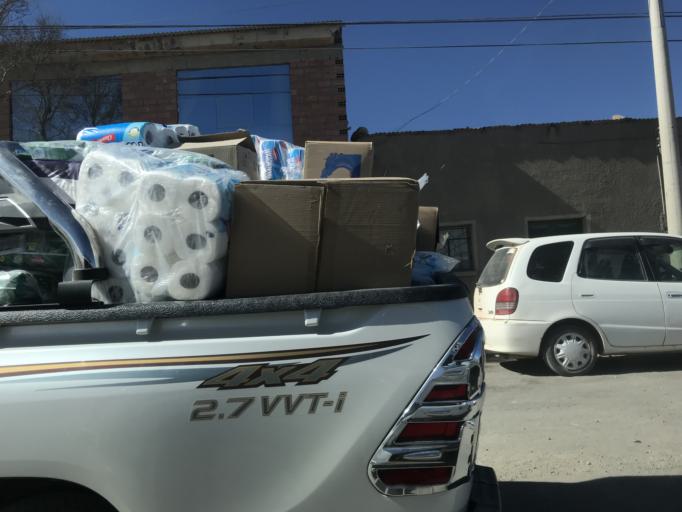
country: BO
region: Potosi
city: Uyuni
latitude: -20.4680
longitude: -66.8258
